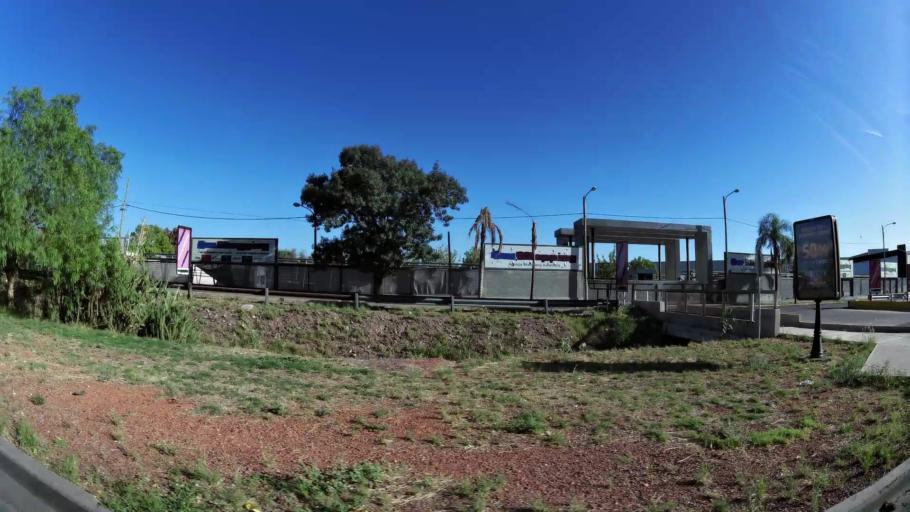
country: AR
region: Mendoza
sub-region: Departamento de Godoy Cruz
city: Godoy Cruz
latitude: -32.9278
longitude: -68.8359
